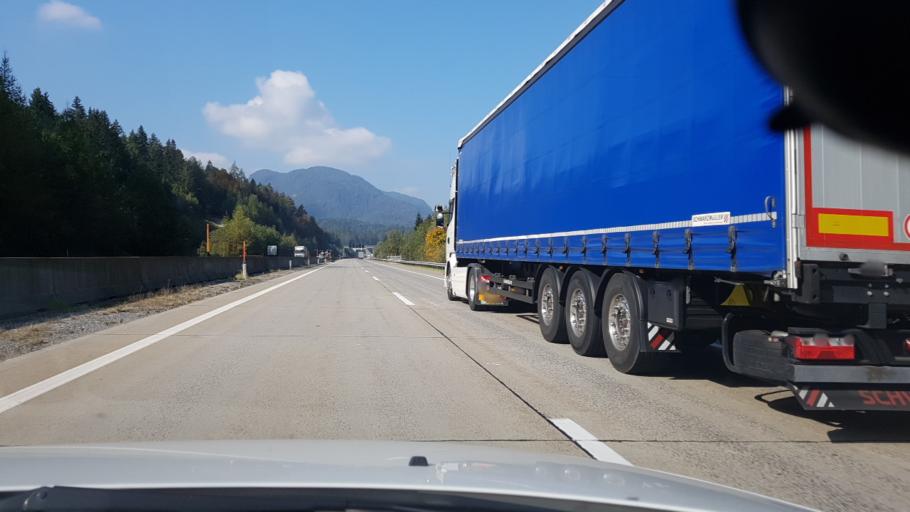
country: AT
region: Carinthia
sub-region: Politischer Bezirk Villach Land
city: Fresach
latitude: 46.6497
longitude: 13.7541
